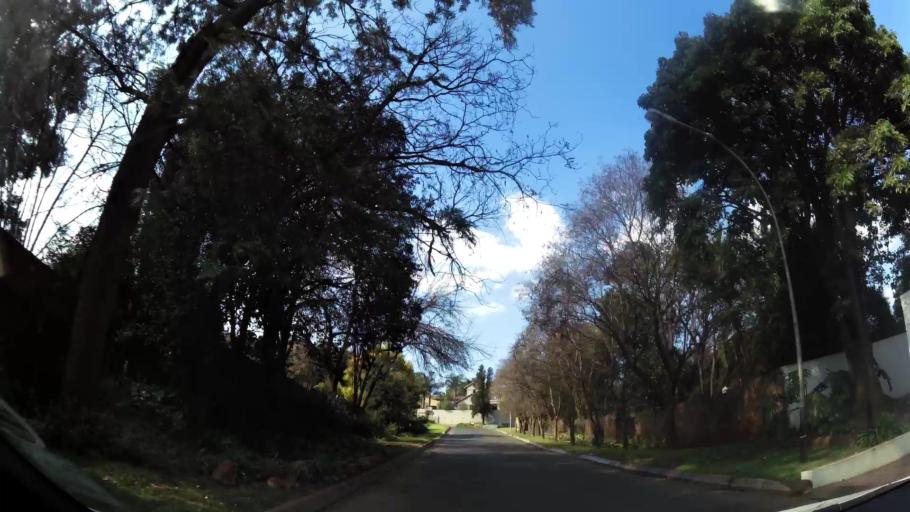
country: ZA
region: Gauteng
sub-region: Ekurhuleni Metropolitan Municipality
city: Germiston
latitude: -26.1928
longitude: 28.1354
